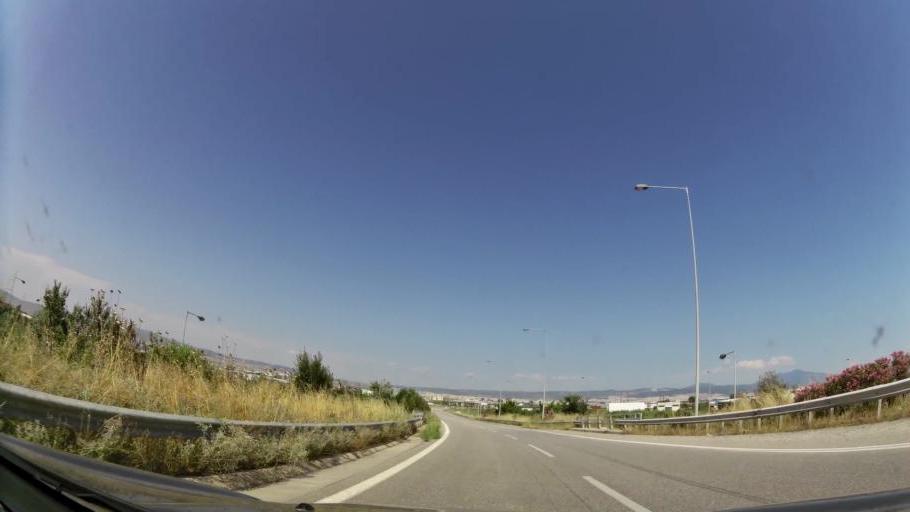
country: GR
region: Central Macedonia
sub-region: Nomos Thessalonikis
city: Kalochori
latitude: 40.6518
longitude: 22.8432
